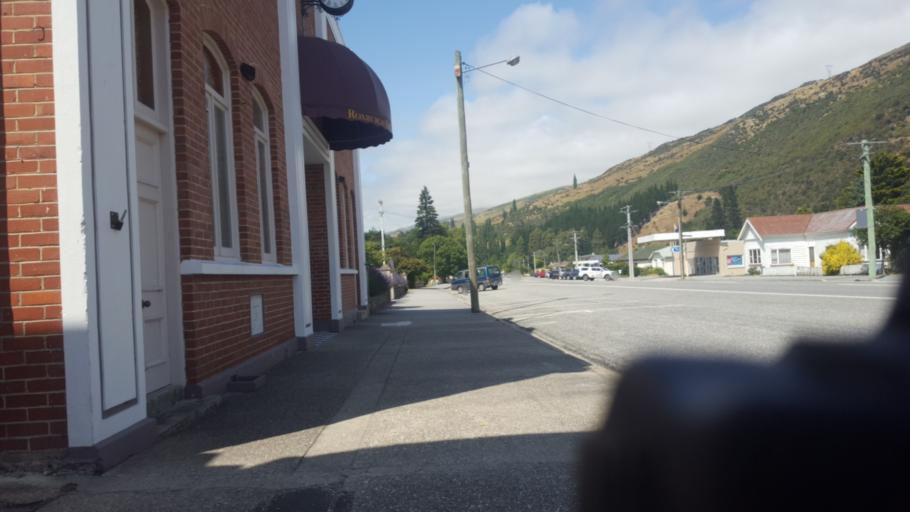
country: NZ
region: Otago
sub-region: Queenstown-Lakes District
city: Kingston
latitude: -45.5423
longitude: 169.3152
